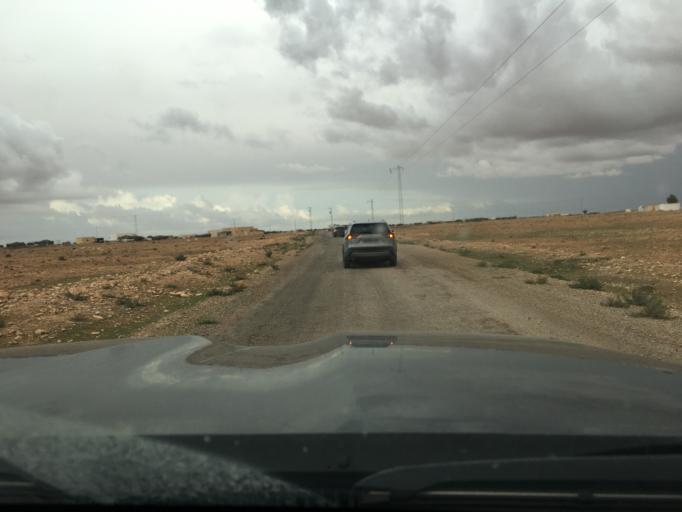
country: TN
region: Madanin
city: Medenine
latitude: 33.2905
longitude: 10.6062
